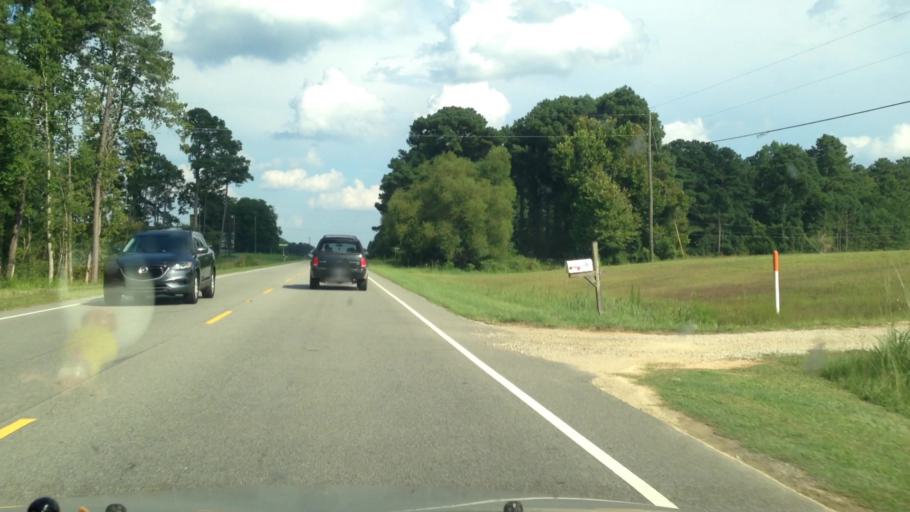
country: US
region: North Carolina
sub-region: Harnett County
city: Lillington
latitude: 35.4159
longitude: -78.8730
